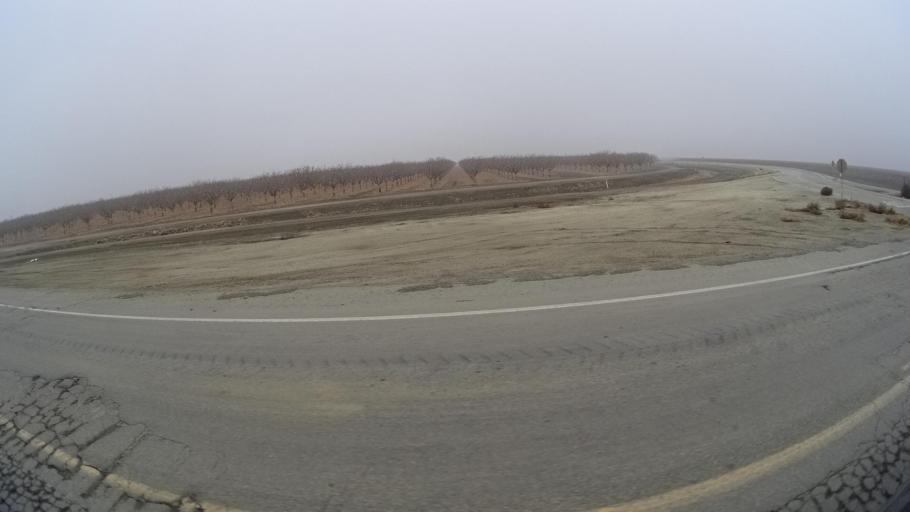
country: US
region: California
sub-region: Kern County
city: Buttonwillow
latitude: 35.4194
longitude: -119.5186
